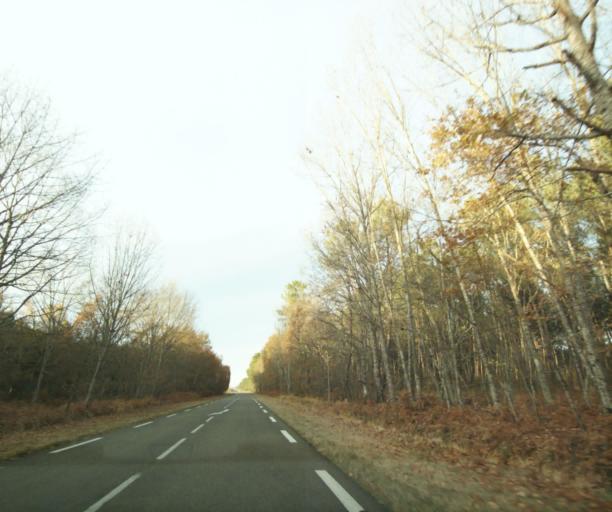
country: FR
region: Aquitaine
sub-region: Departement de la Gironde
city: Grignols
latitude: 44.1940
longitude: -0.1548
